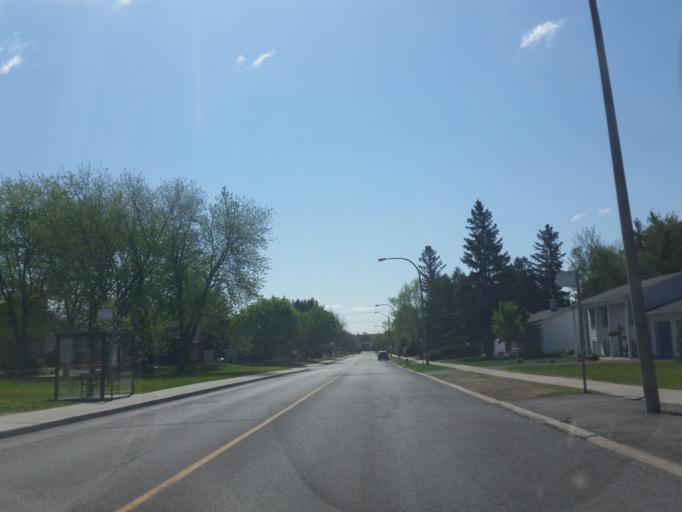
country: CA
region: Ontario
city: Ottawa
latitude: 45.3512
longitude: -75.7204
